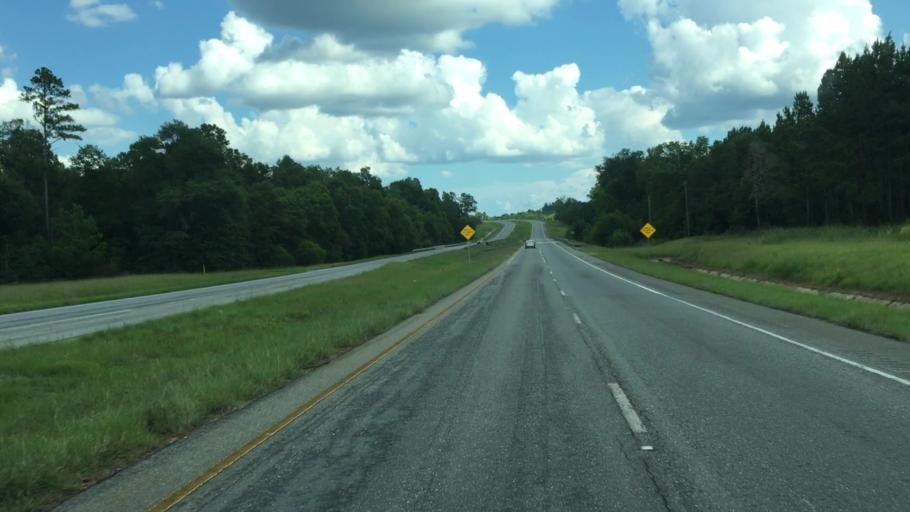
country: US
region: Georgia
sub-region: Wilkinson County
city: Irwinton
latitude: 32.7013
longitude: -83.1233
